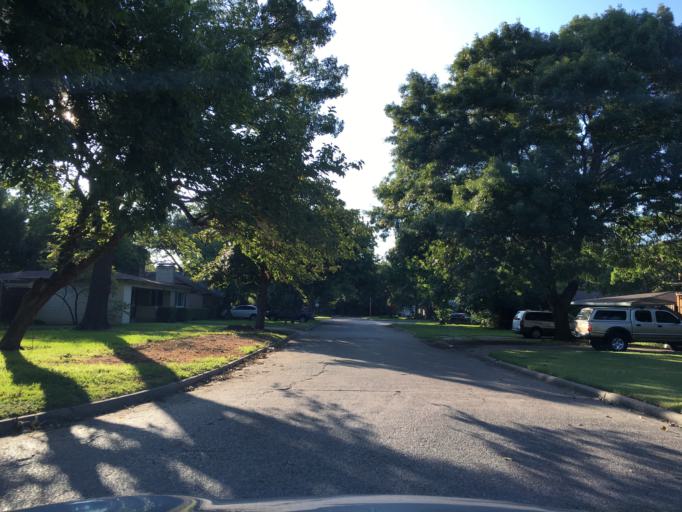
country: US
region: Texas
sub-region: Dallas County
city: Highland Park
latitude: 32.8556
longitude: -96.7397
